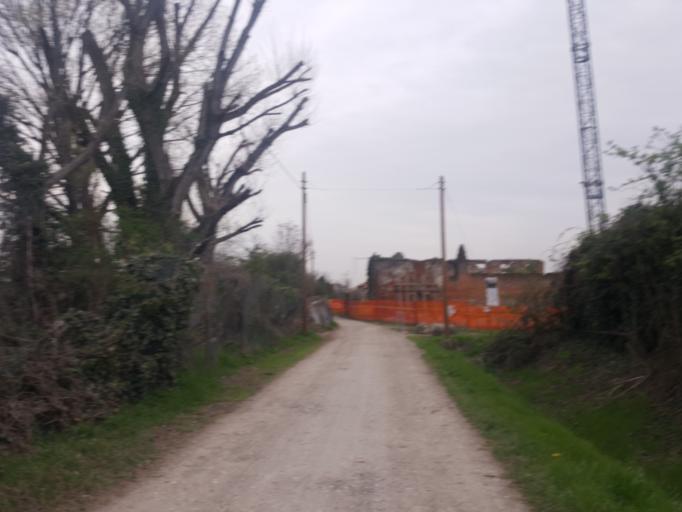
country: IT
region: Lombardy
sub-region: Citta metropolitana di Milano
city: Romano Banco
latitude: 45.4304
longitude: 9.1291
